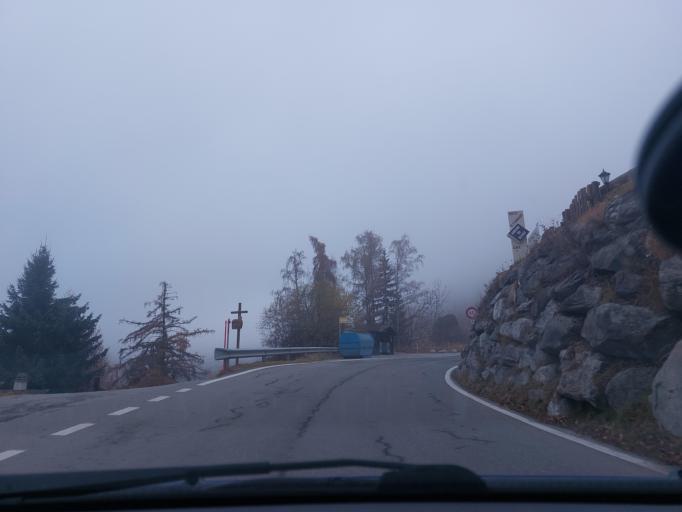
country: CH
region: Valais
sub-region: Conthey District
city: Basse-Nendaz
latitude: 46.1719
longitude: 7.3116
